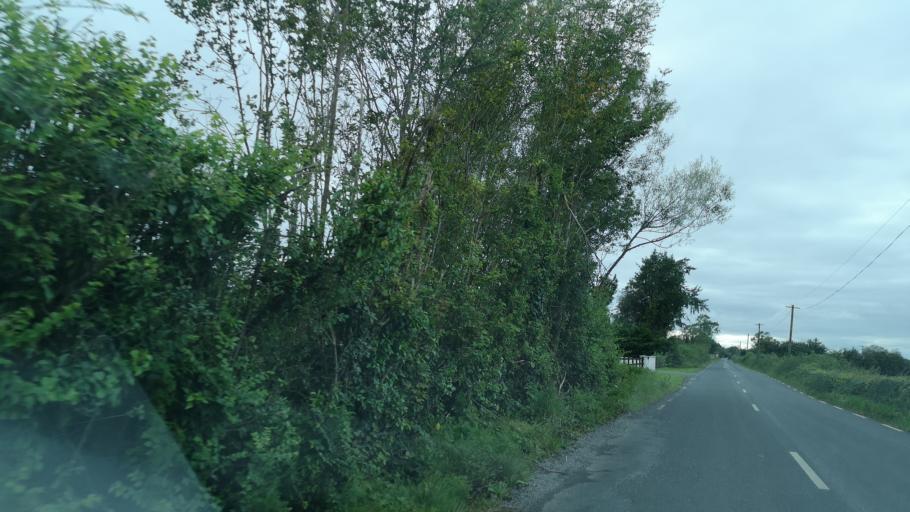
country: IE
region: Leinster
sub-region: Uibh Fhaili
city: Ferbane
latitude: 53.2260
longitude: -7.8099
